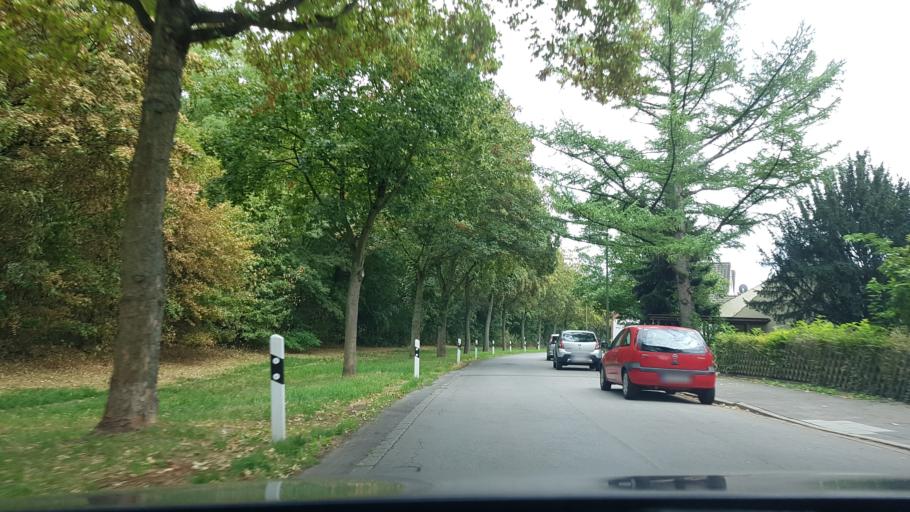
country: DE
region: North Rhine-Westphalia
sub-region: Regierungsbezirk Dusseldorf
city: Hochfeld
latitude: 51.4198
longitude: 6.7152
